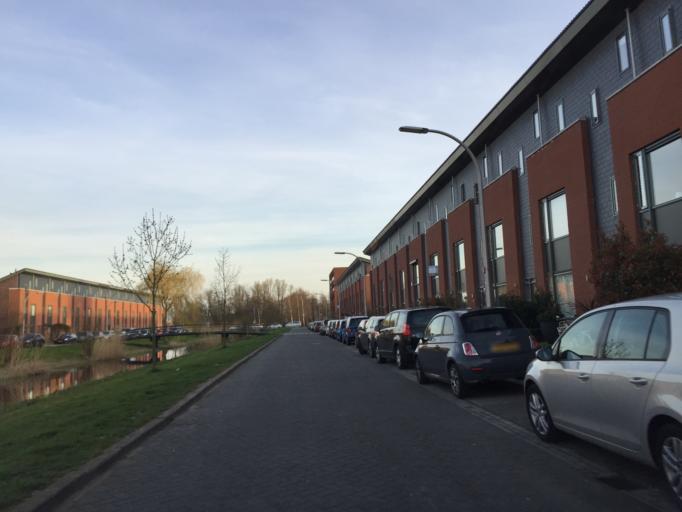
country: NL
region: South Holland
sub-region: Gemeente Pijnacker-Nootdorp
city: Pijnacker
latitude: 52.0089
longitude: 4.4487
